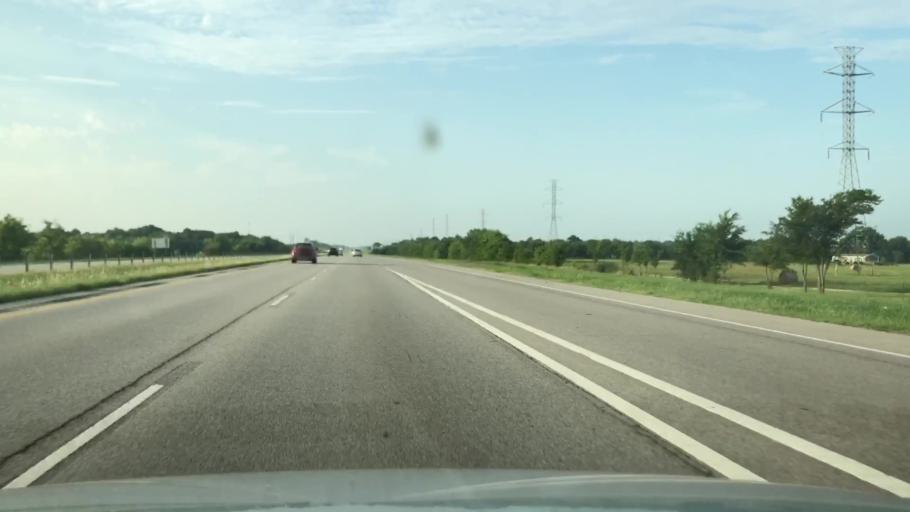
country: US
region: Oklahoma
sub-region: Tulsa County
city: Sperry
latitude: 36.3182
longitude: -95.9245
